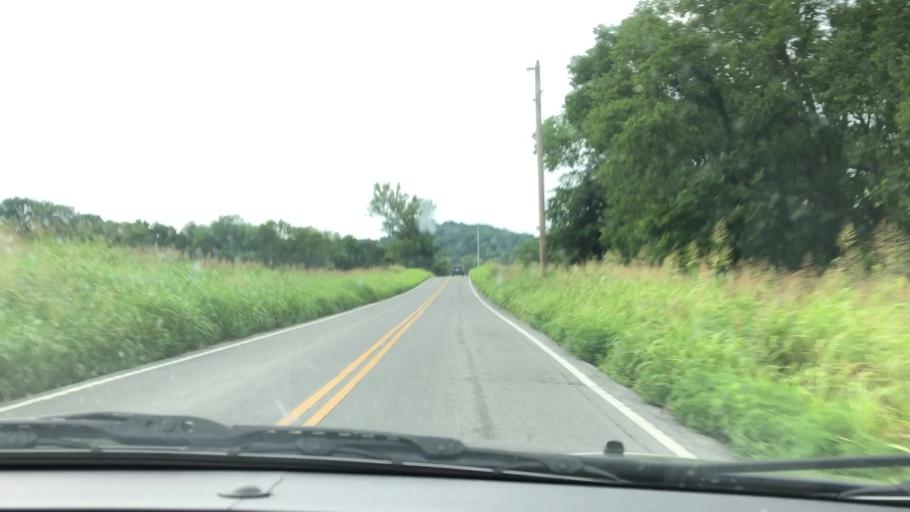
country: US
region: Tennessee
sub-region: Maury County
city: Spring Hill
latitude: 35.7855
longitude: -87.0042
